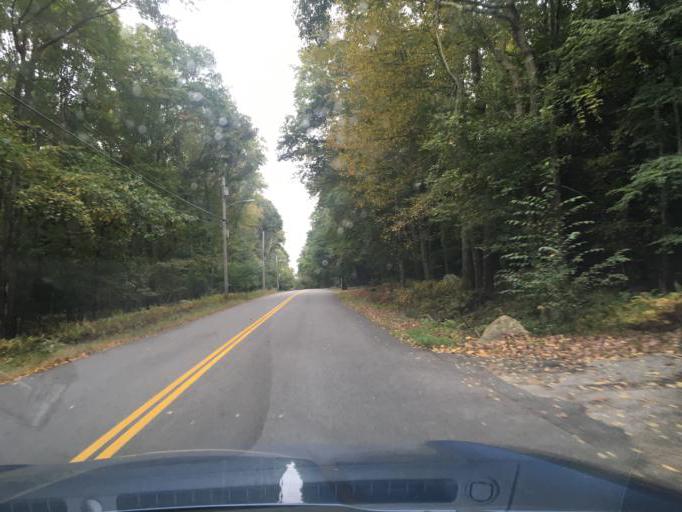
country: US
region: Rhode Island
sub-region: Washington County
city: Exeter
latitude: 41.6168
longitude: -71.5370
